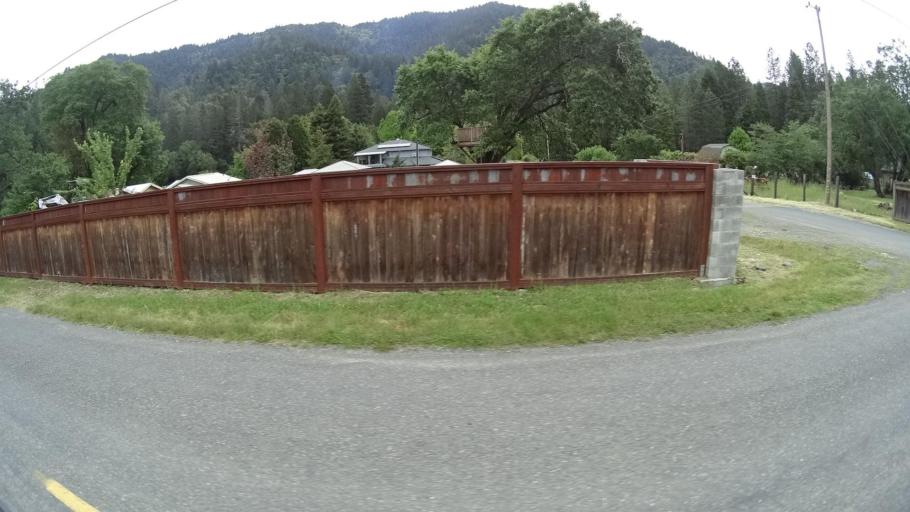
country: US
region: California
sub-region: Humboldt County
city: Willow Creek
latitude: 40.9609
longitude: -123.6304
